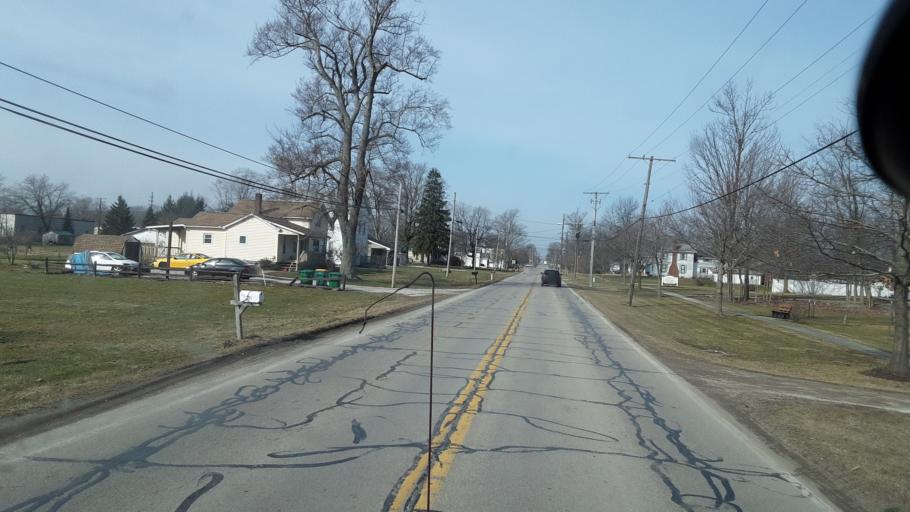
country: US
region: Ohio
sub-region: Ashtabula County
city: Jefferson
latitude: 41.7384
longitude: -80.7565
